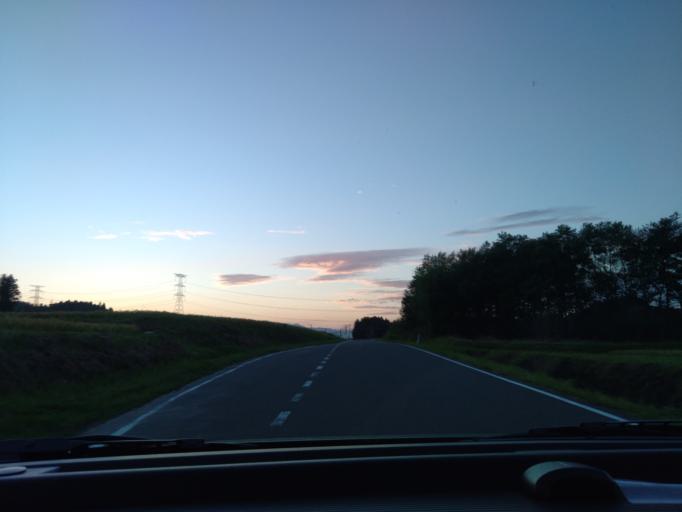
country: JP
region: Iwate
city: Ichinoseki
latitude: 38.8567
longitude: 141.1462
